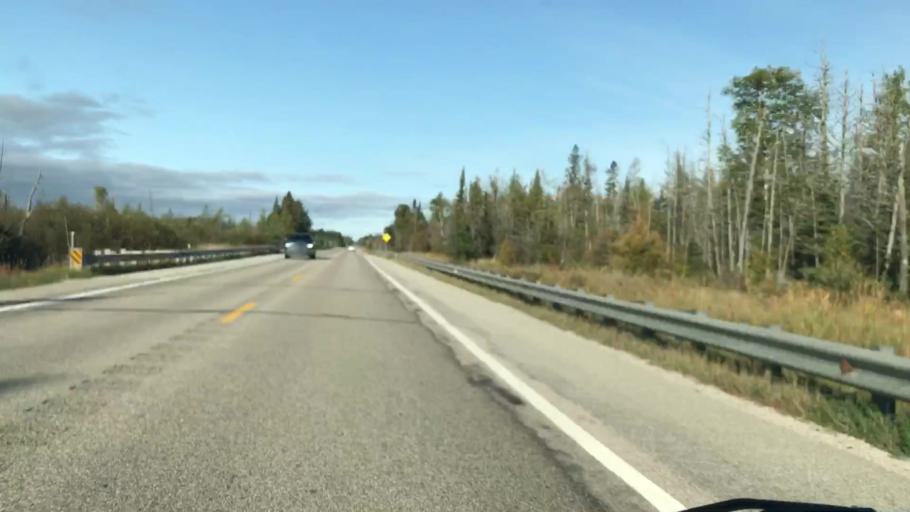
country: US
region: Michigan
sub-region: Luce County
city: Newberry
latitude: 46.3036
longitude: -85.3174
